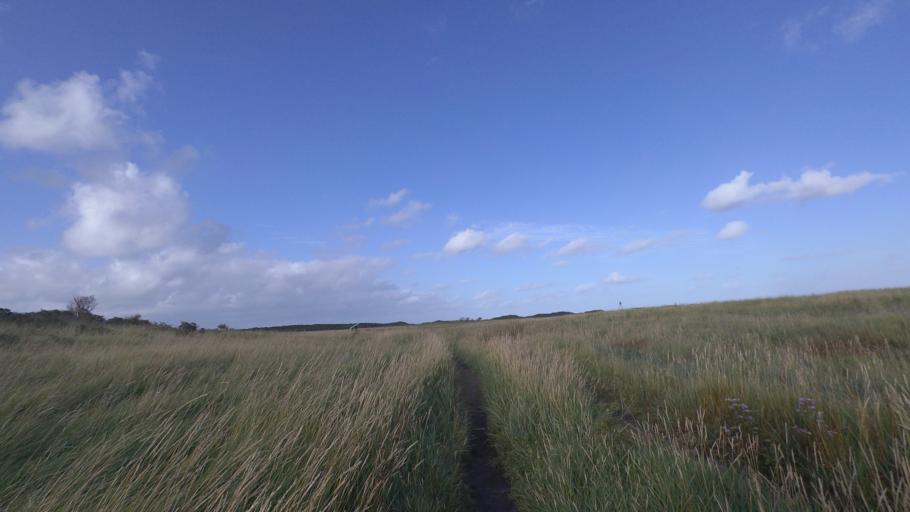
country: NL
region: Friesland
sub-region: Gemeente Dongeradeel
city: Ternaard
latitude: 53.4598
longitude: 5.9198
